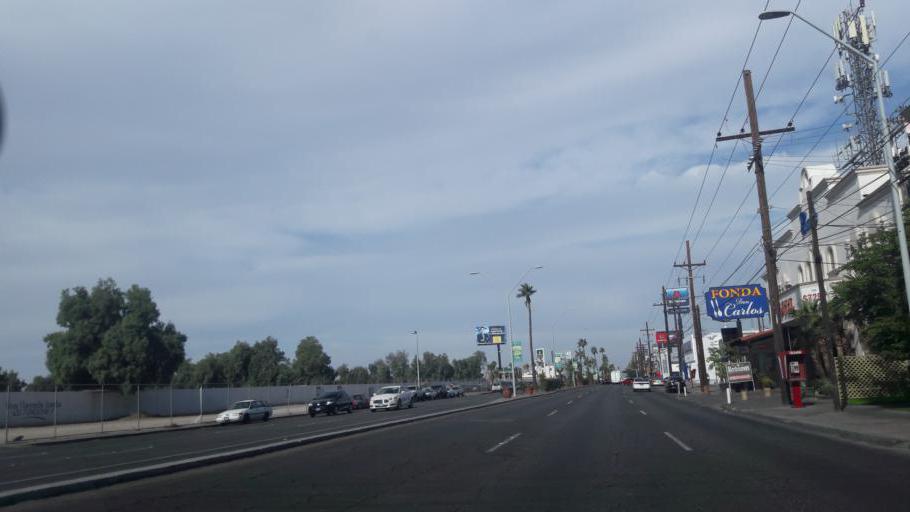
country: MX
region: Baja California
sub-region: Mexicali
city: Mexicali
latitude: 32.6506
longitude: -115.4523
